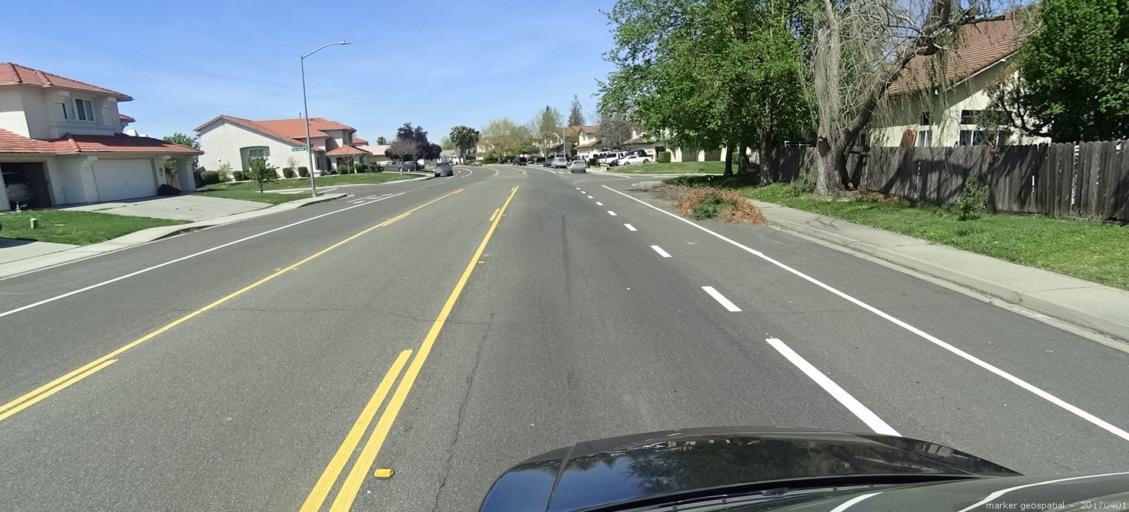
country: US
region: California
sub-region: Sacramento County
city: Laguna
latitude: 38.4443
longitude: -121.4377
